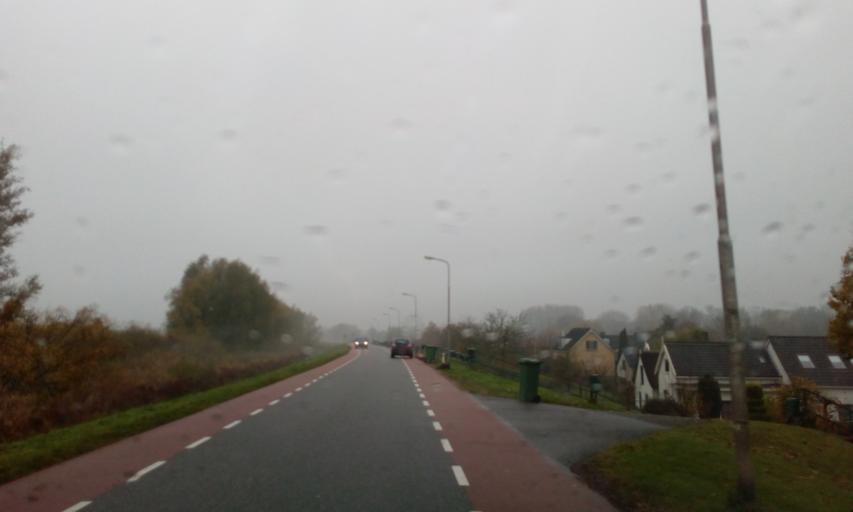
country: NL
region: South Holland
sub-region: Molenwaard
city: Nieuw-Lekkerland
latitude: 51.8919
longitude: 4.6636
